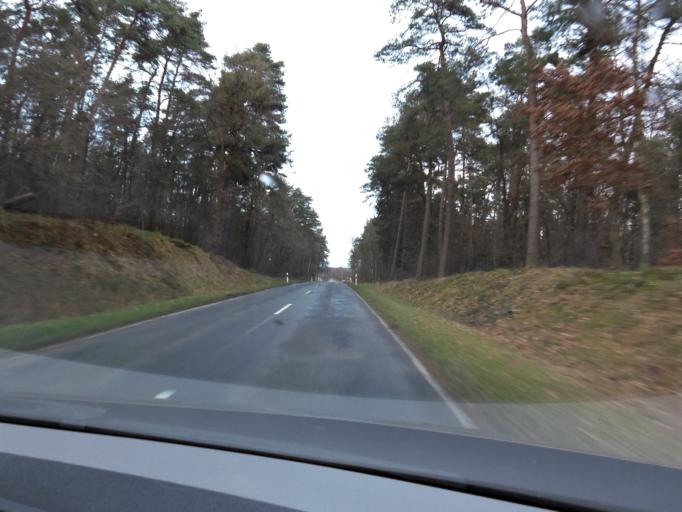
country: DE
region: Schleswig-Holstein
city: Seedorf
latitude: 53.6429
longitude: 10.8608
